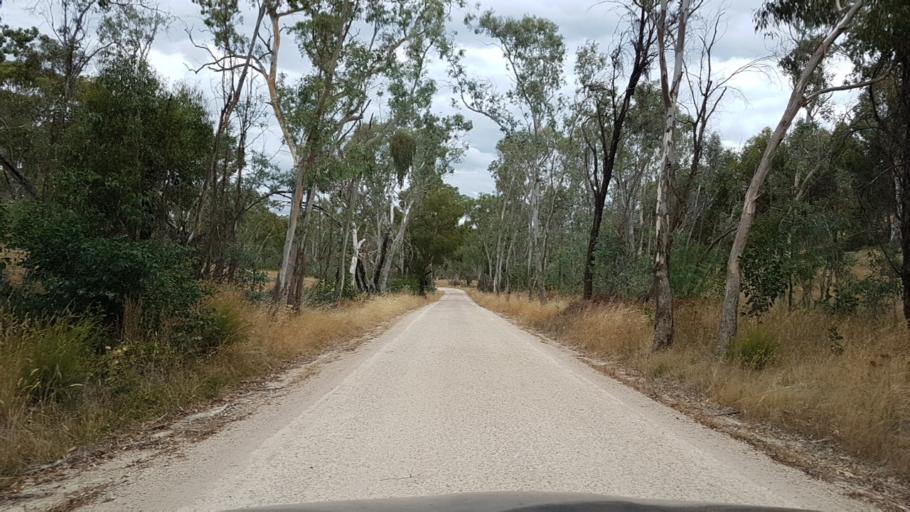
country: AU
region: South Australia
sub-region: Adelaide Hills
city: Gumeracha
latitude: -34.8045
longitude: 138.8338
